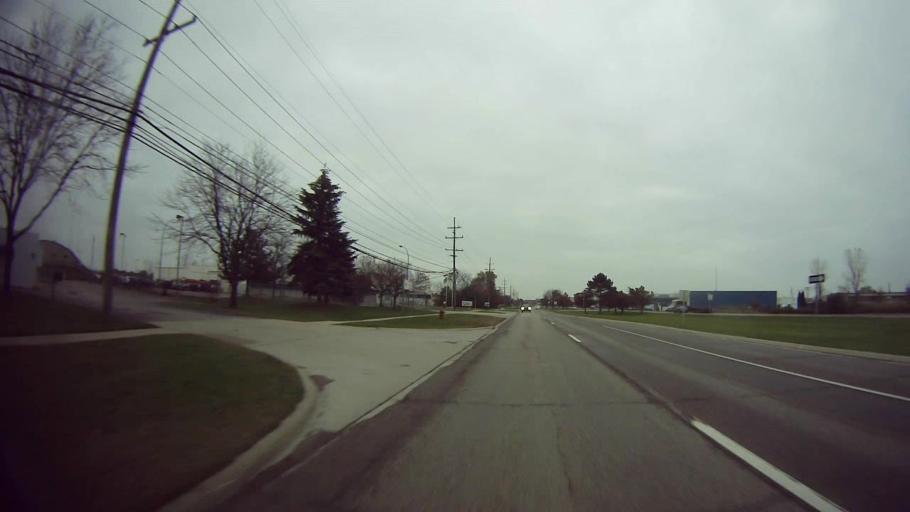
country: US
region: Michigan
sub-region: Oakland County
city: Clawson
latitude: 42.5528
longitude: -83.1247
